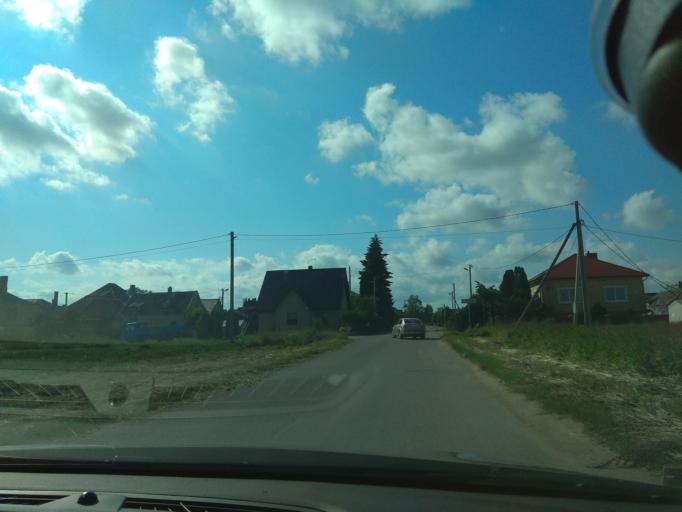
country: LT
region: Siauliu apskritis
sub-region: Joniskis
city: Joniskis
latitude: 56.2444
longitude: 23.6272
